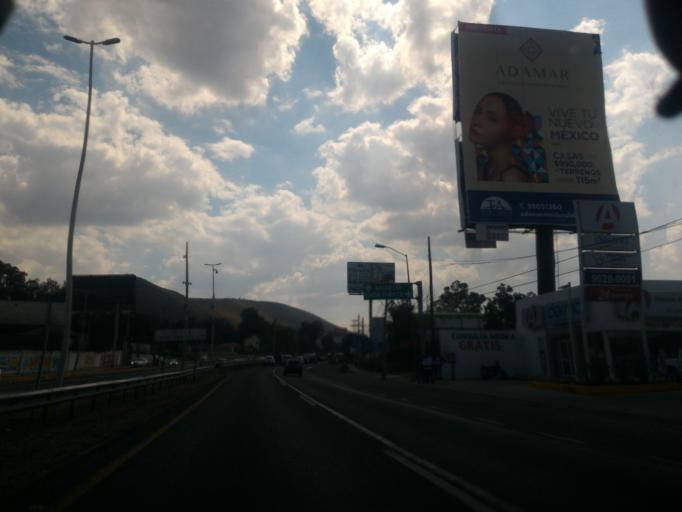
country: MX
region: Jalisco
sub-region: Tlajomulco de Zuniga
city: Lomas de San Agustin
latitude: 20.5339
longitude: -103.4752
